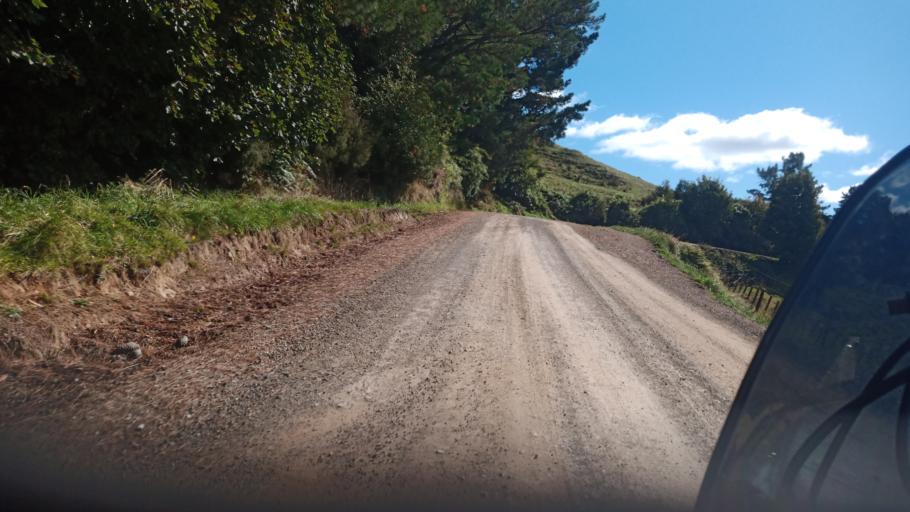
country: NZ
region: Bay of Plenty
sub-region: Opotiki District
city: Opotiki
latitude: -38.3340
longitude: 177.5776
